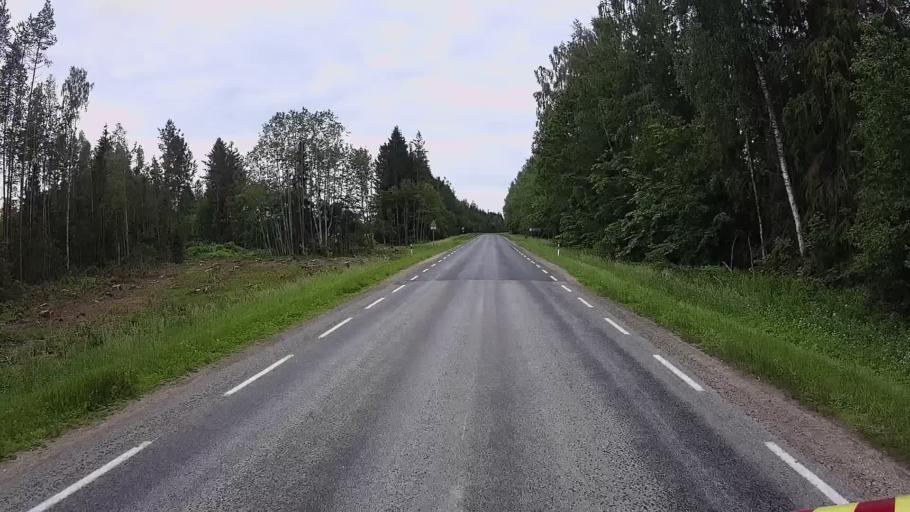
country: EE
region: Viljandimaa
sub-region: Karksi vald
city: Karksi-Nuia
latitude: 58.2081
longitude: 25.6211
